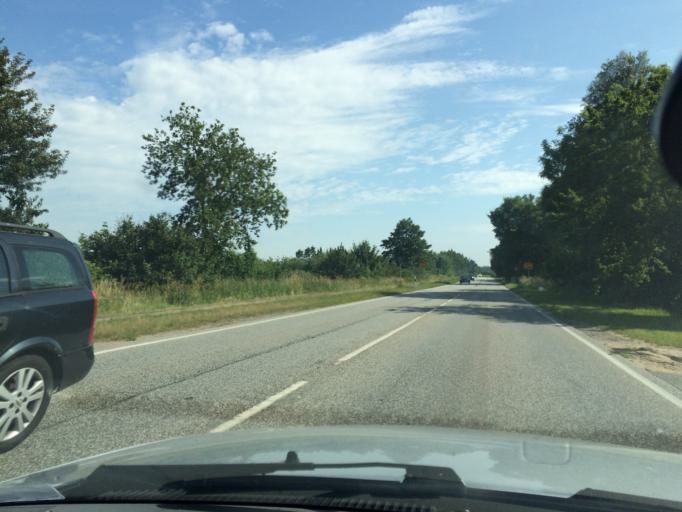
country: DE
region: Schleswig-Holstein
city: Jarplund-Weding
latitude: 54.7362
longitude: 9.4414
